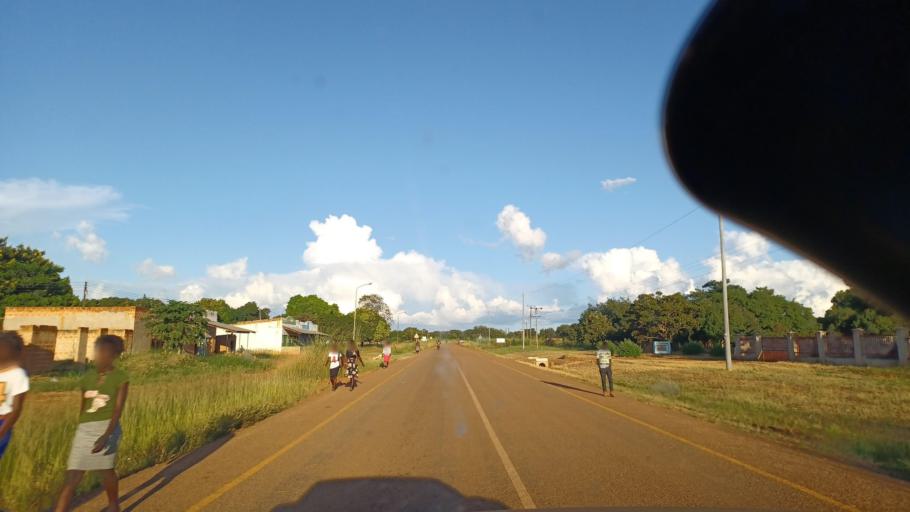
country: ZM
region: North-Western
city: Kalengwa
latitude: -13.1381
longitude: 25.0127
